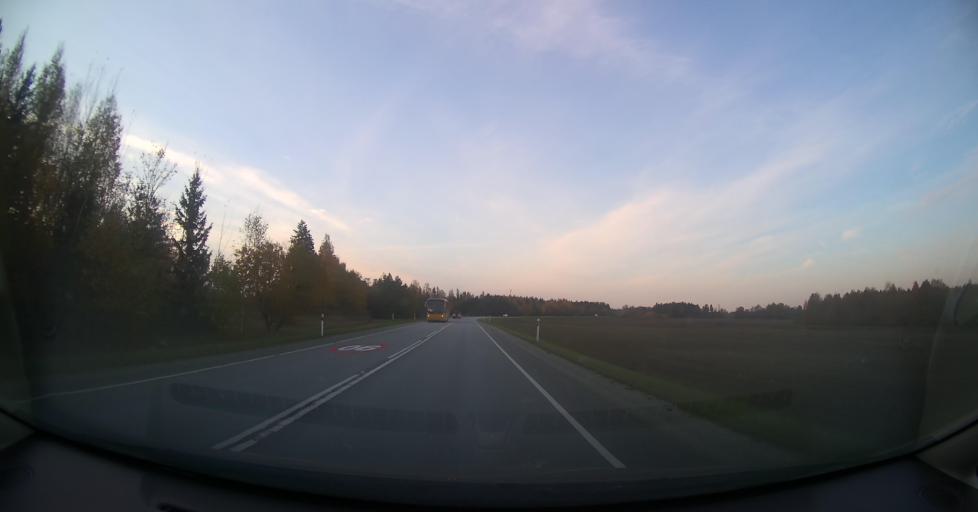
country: EE
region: Harju
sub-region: Nissi vald
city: Riisipere
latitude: 59.1373
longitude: 24.3315
